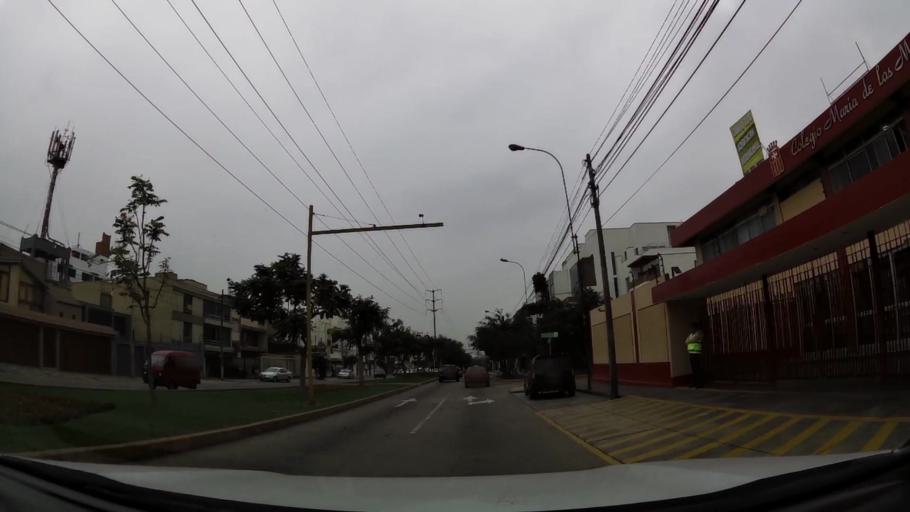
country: PE
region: Lima
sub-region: Lima
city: Surco
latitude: -12.1297
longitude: -77.0096
